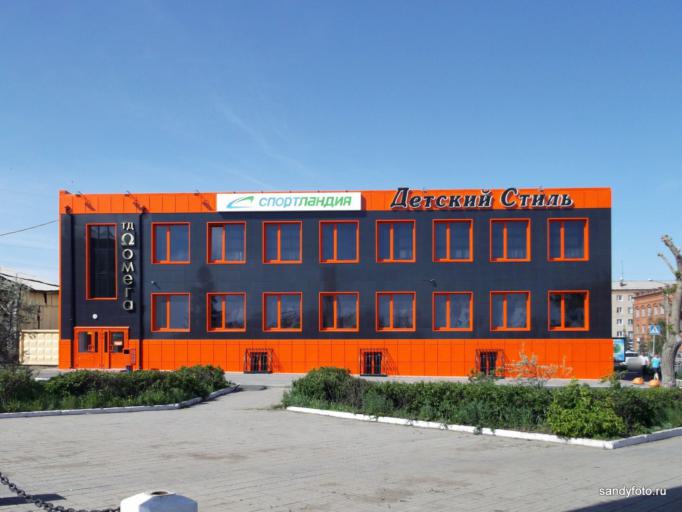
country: RU
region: Chelyabinsk
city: Troitsk
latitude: 54.0904
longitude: 61.5657
